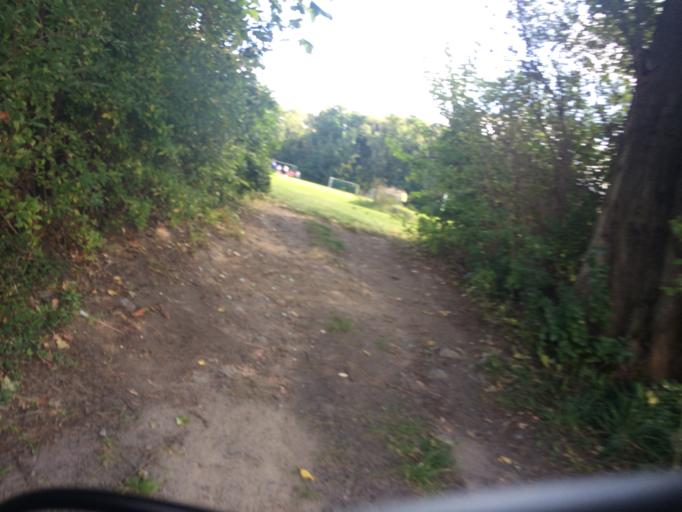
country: DE
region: Berlin
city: Weissensee
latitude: 52.5636
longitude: 13.4573
